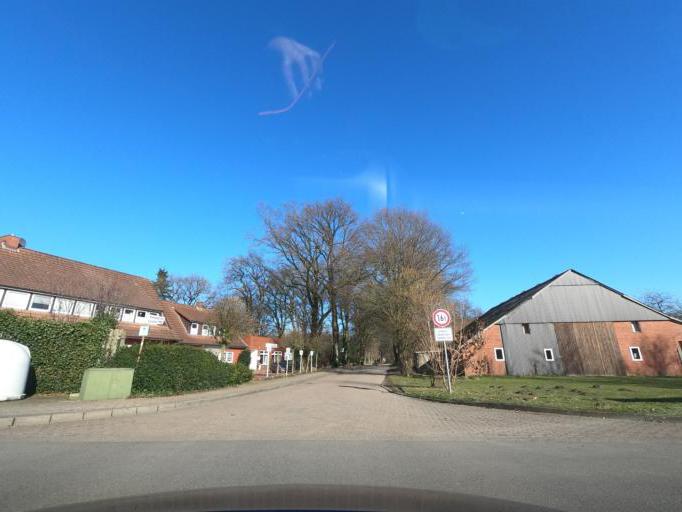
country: DE
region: Lower Saxony
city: Emstek
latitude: 52.8525
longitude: 8.1434
